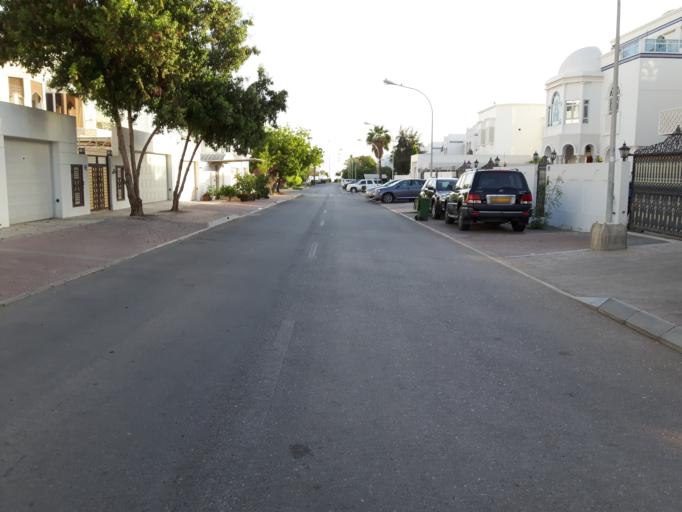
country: OM
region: Muhafazat Masqat
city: Bawshar
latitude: 23.6099
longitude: 58.4489
